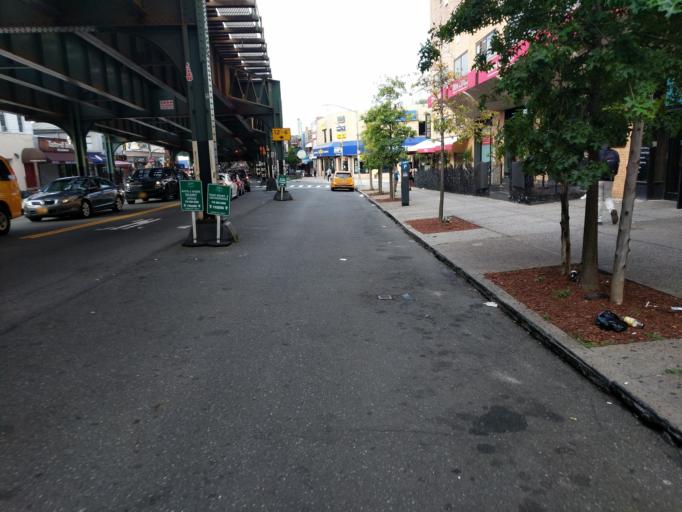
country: US
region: New York
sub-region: Queens County
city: Long Island City
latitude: 40.7682
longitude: -73.9203
